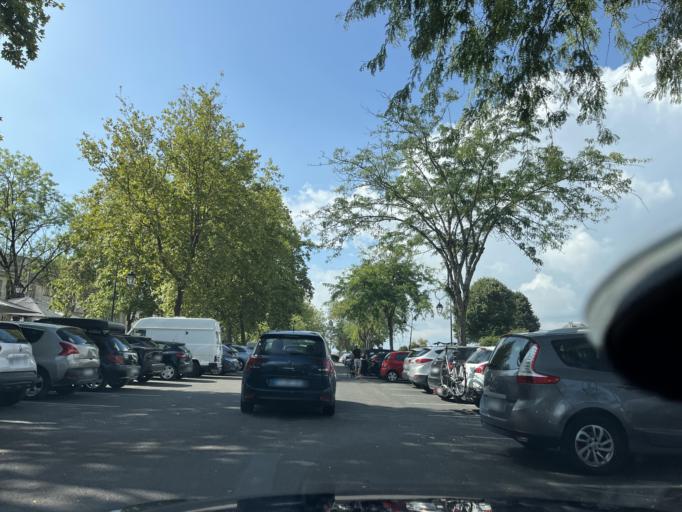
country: FR
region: Aquitaine
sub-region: Departement de la Gironde
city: Blaye
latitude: 45.1287
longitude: -0.6627
